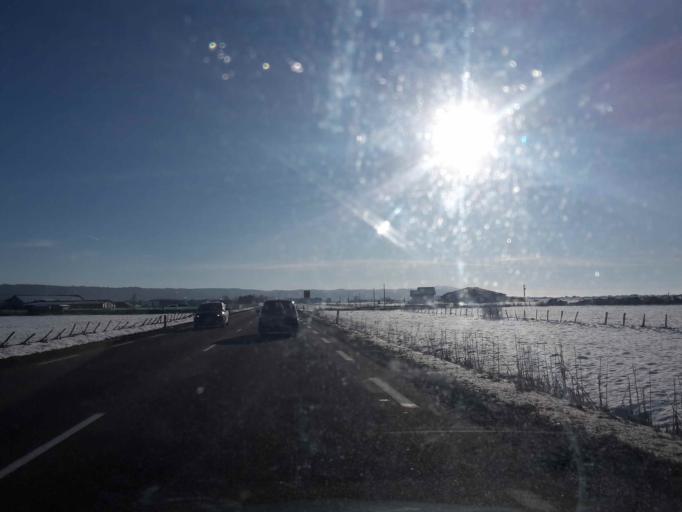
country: FR
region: Franche-Comte
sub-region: Departement du Doubs
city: Doubs
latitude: 46.9321
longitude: 6.3418
